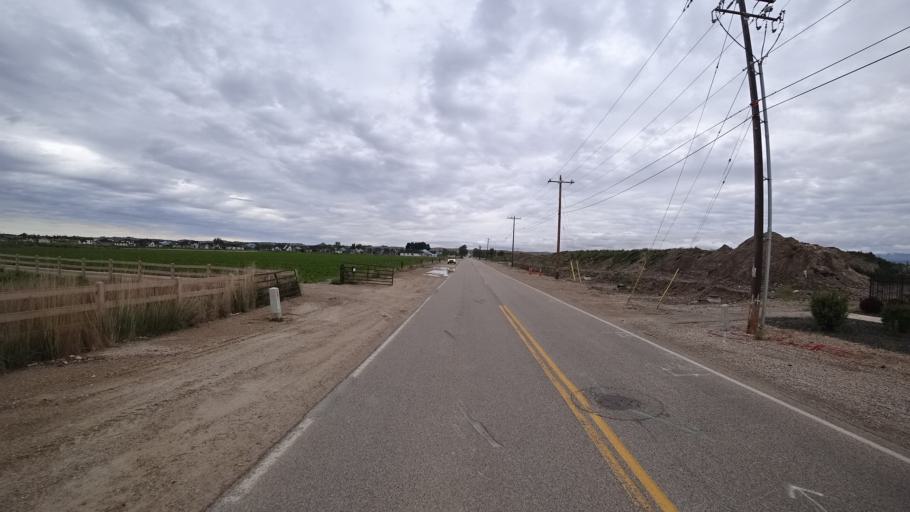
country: US
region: Idaho
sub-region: Ada County
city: Star
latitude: 43.6996
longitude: -116.4435
